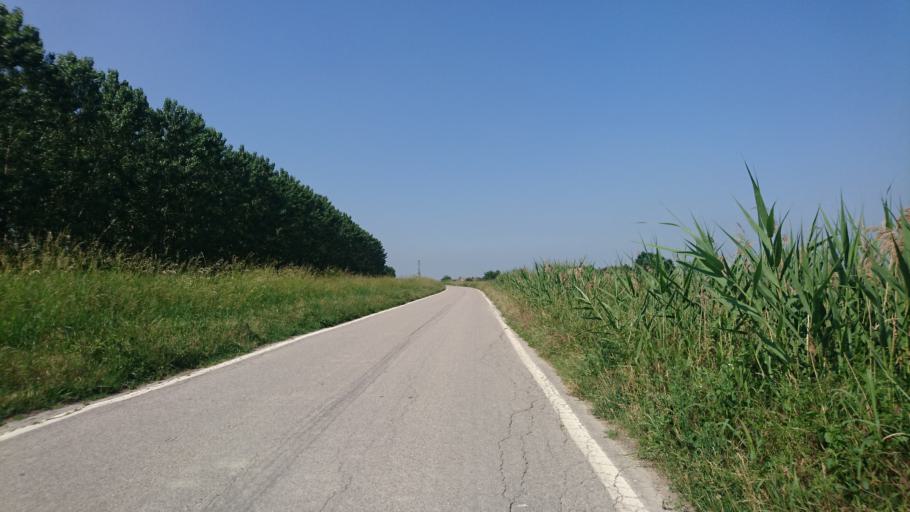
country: IT
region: Lombardy
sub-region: Provincia di Mantova
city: Serravalle a Po
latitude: 45.0746
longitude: 11.1079
